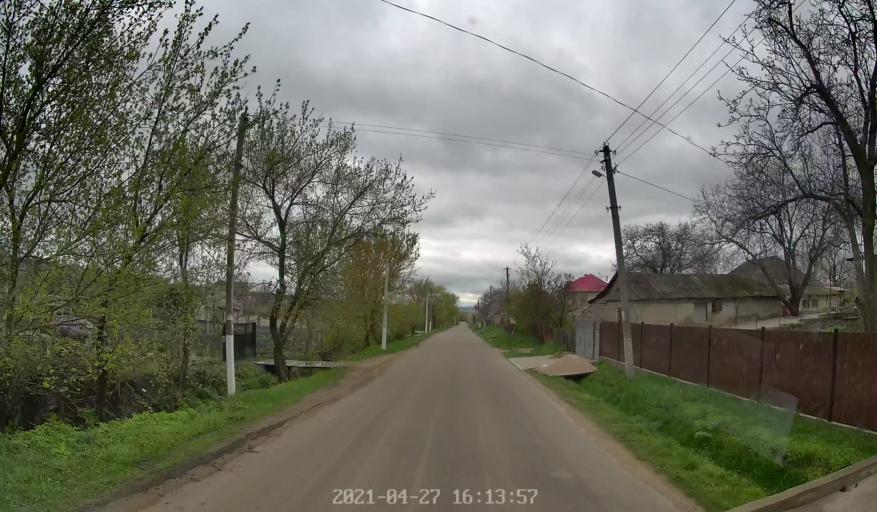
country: MD
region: Chisinau
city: Singera
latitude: 47.0058
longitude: 29.0141
